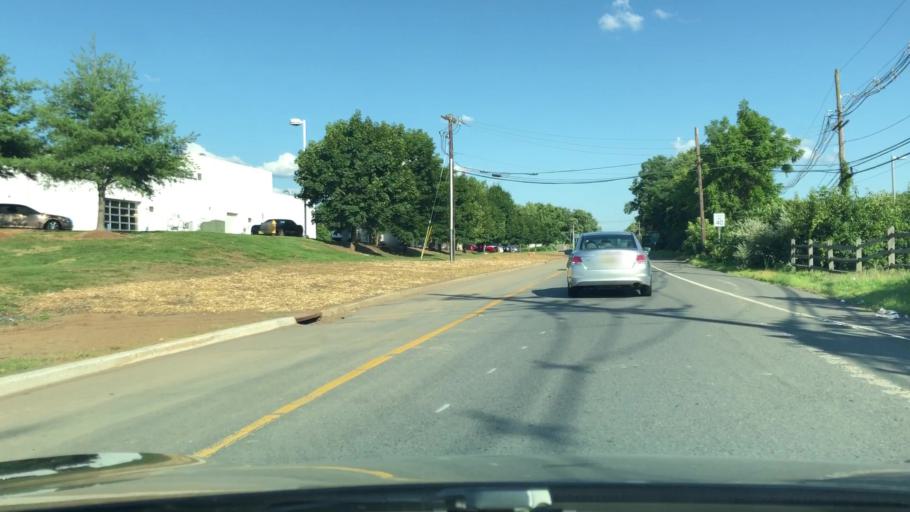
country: US
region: New Jersey
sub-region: Mercer County
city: Lawrenceville
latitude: 40.2888
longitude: -74.6890
